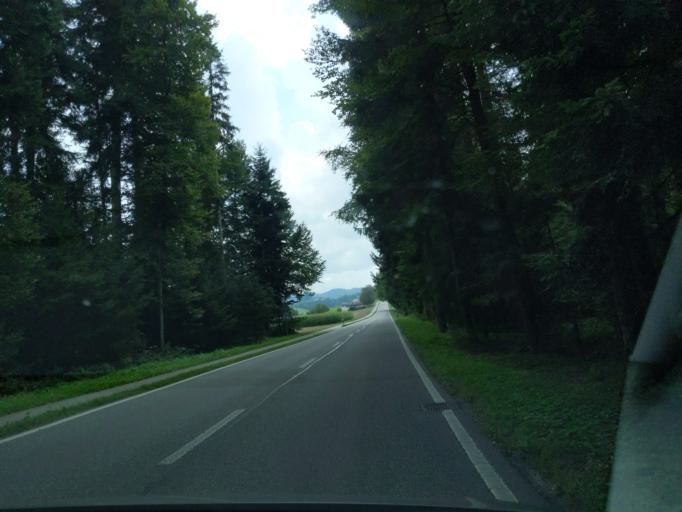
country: CH
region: Bern
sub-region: Oberaargau
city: Wyssachen
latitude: 47.1008
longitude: 7.8277
